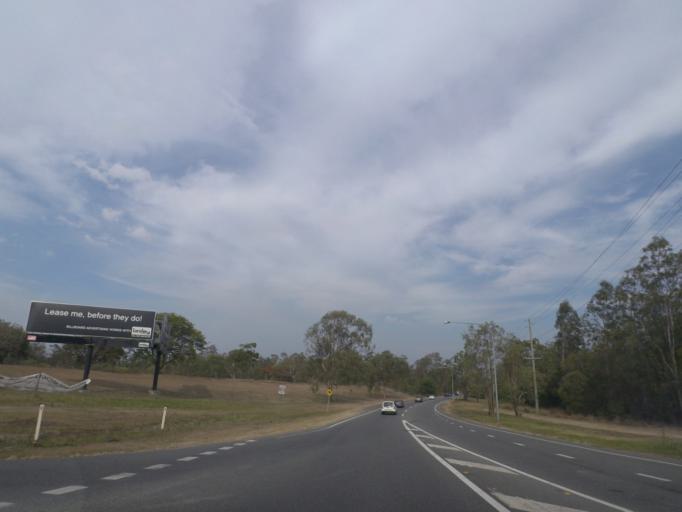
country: AU
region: Queensland
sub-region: Brisbane
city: Inala
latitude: -27.5930
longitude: 152.9936
